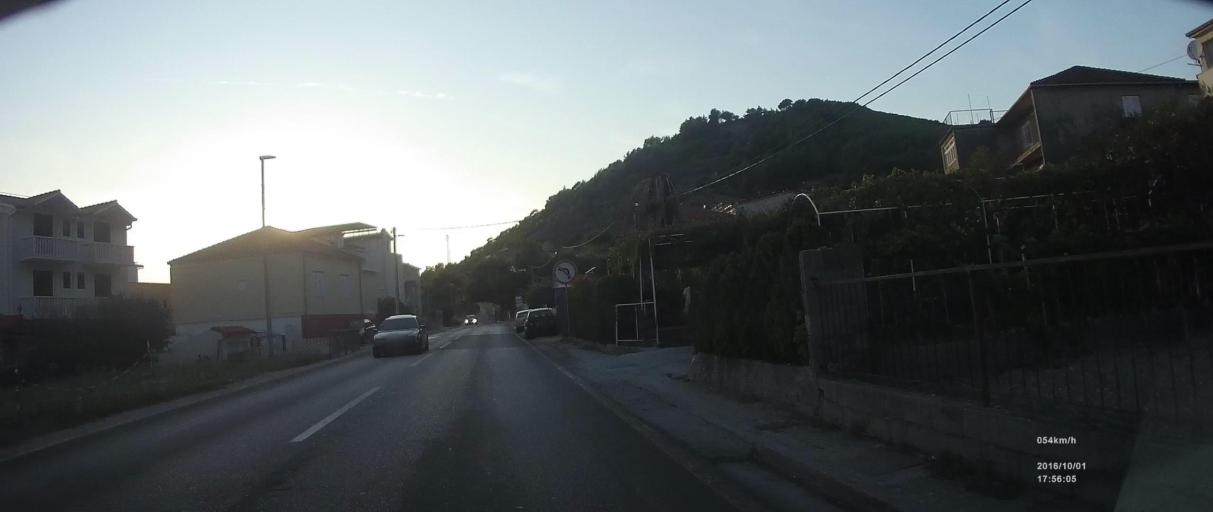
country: HR
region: Splitsko-Dalmatinska
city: Srinjine
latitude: 43.4647
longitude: 16.5864
